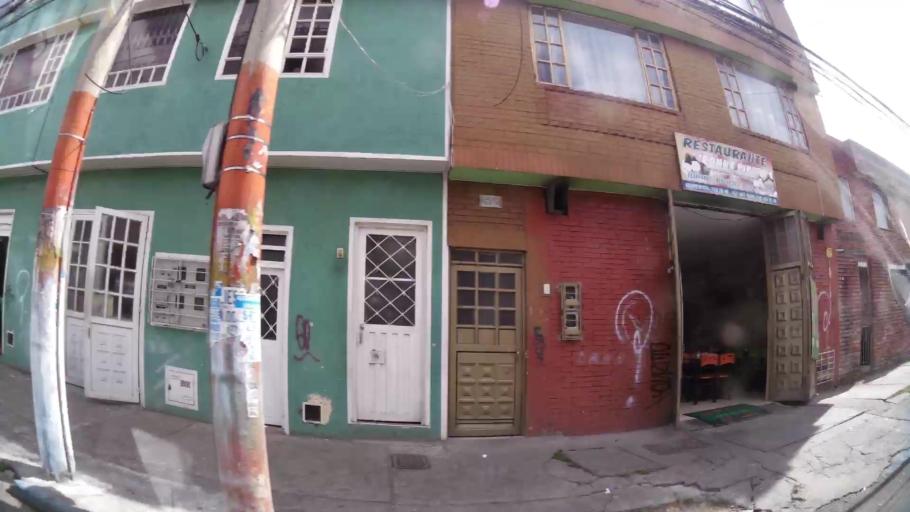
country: CO
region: Bogota D.C.
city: Bogota
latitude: 4.6972
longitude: -74.1105
